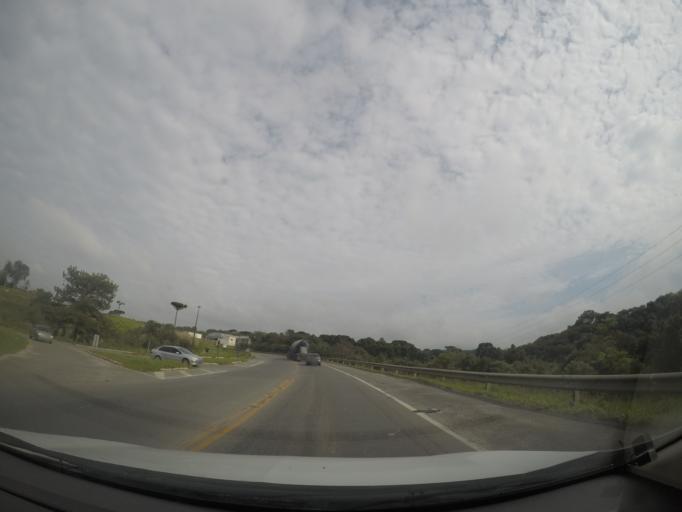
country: BR
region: Parana
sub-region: Colombo
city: Colombo
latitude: -25.3347
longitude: -49.2521
